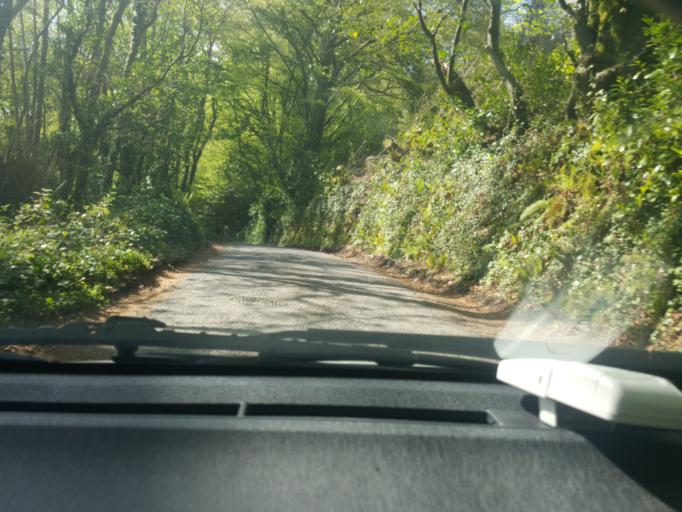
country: IE
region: Munster
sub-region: County Cork
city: Bandon
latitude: 51.7699
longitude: -8.6724
